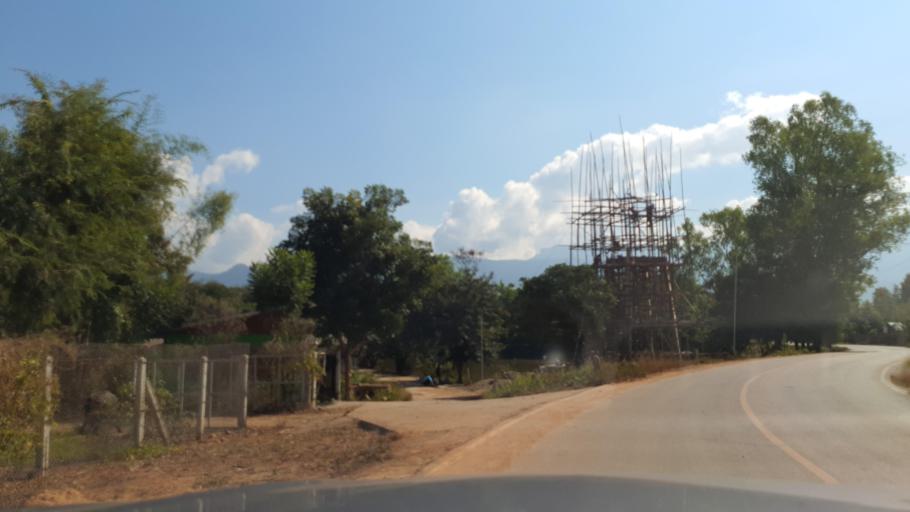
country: TH
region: Nan
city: Pua
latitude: 19.1415
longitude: 100.9243
